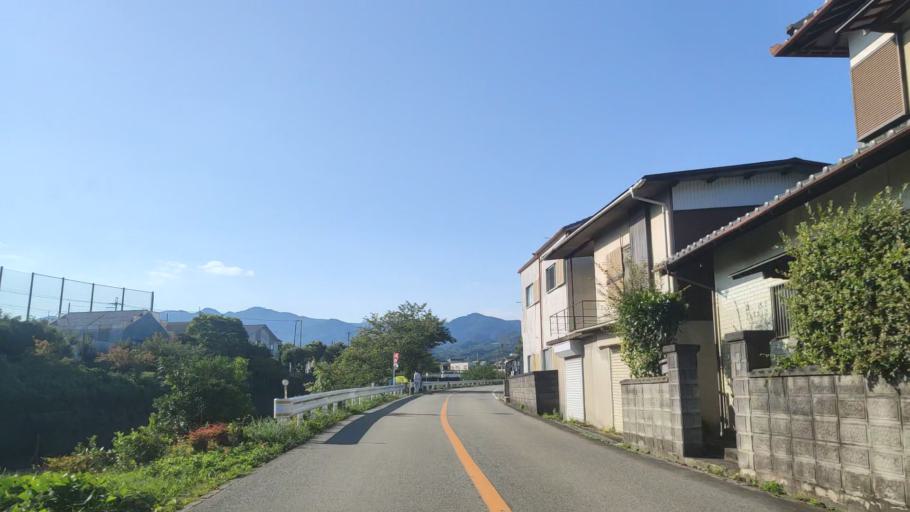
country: JP
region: Hyogo
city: Sandacho
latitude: 34.8295
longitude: 135.2408
